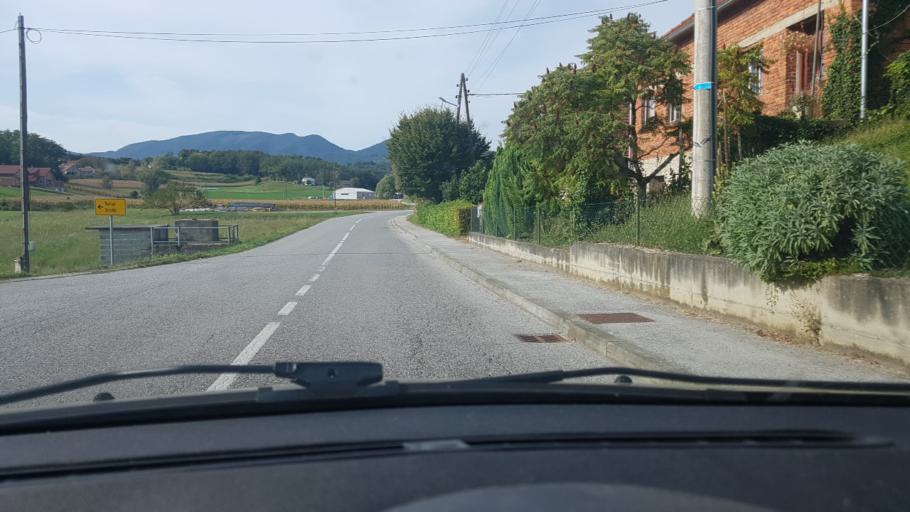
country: HR
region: Krapinsko-Zagorska
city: Mihovljan
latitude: 46.1372
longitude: 15.9661
